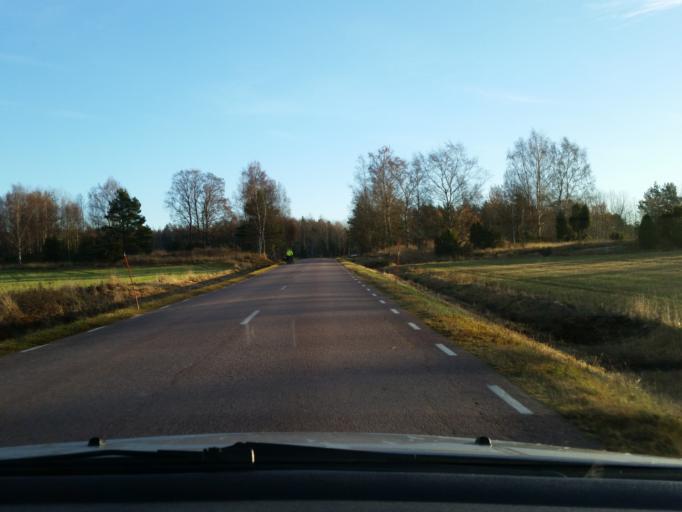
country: AX
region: Alands landsbygd
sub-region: Sund
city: Sund
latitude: 60.2795
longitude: 20.0943
